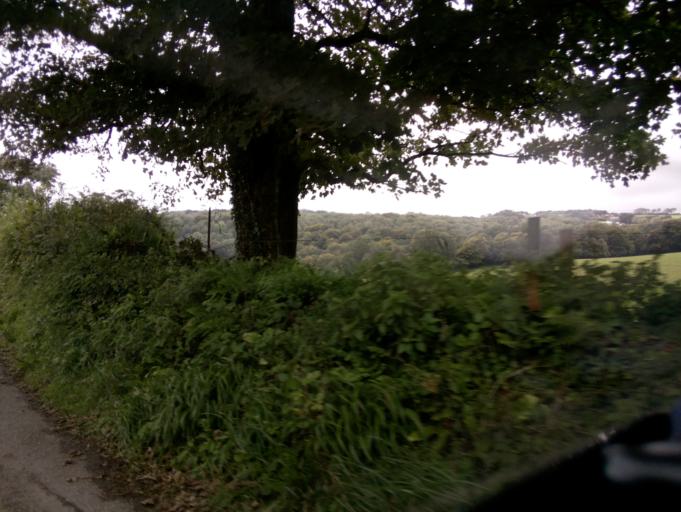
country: GB
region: England
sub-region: Devon
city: Totnes
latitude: 50.3522
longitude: -3.6636
